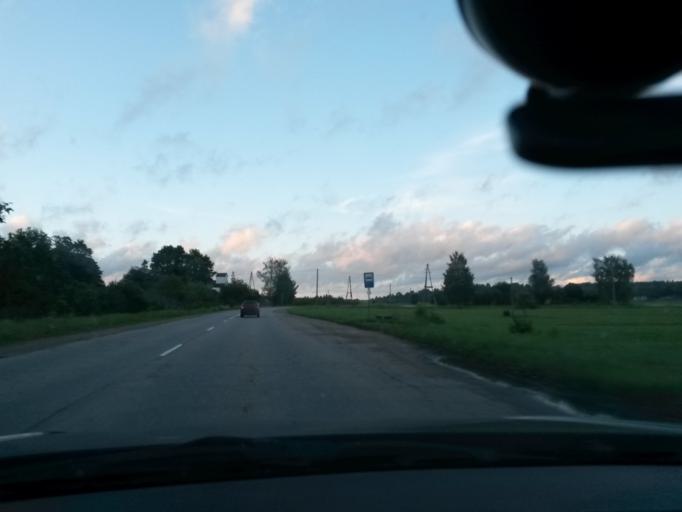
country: LV
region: Madonas Rajons
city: Madona
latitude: 56.7222
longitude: 25.9926
